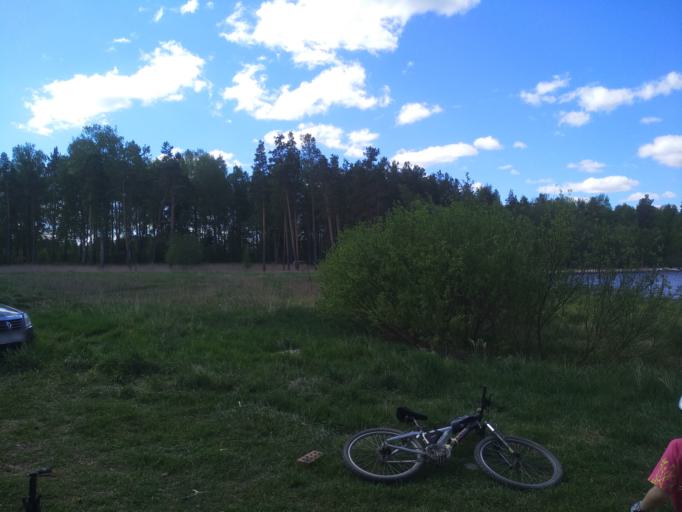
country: RU
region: Leningrad
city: Veshchevo
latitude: 60.7934
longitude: 29.0785
